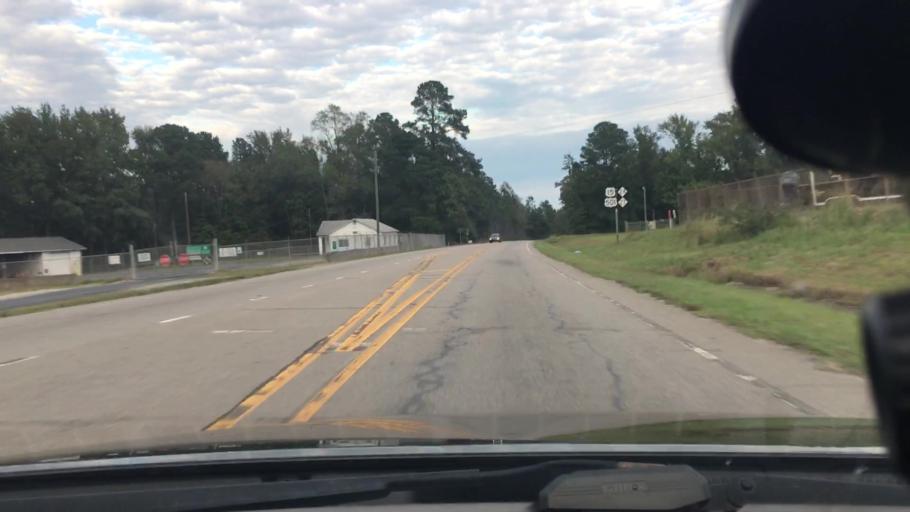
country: US
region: North Carolina
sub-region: Moore County
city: Carthage
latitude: 35.3473
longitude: -79.3815
